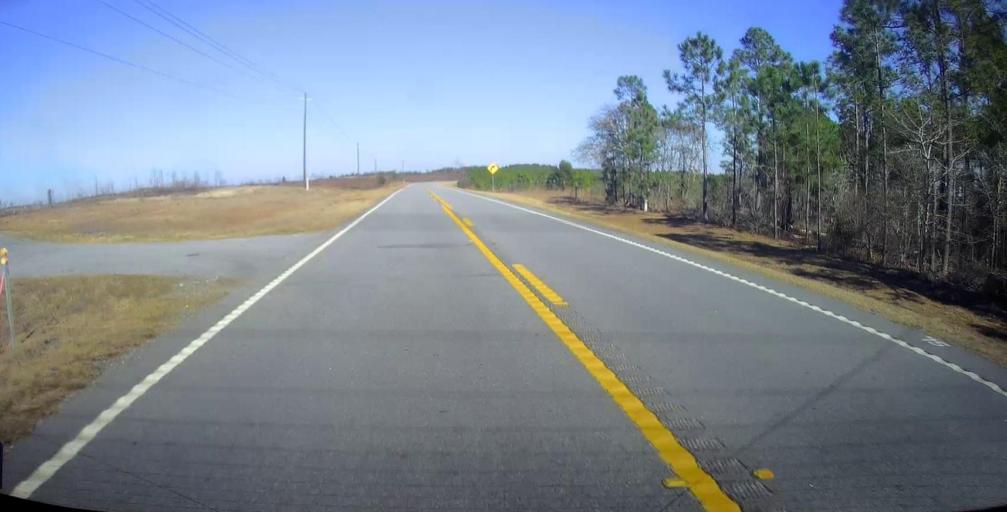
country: US
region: Georgia
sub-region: Taylor County
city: Butler
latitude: 32.5796
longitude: -84.2078
